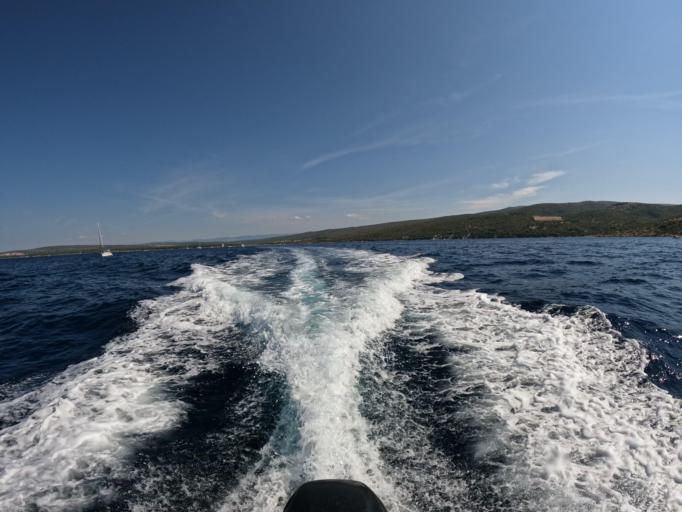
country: HR
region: Primorsko-Goranska
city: Punat
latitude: 44.9870
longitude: 14.6129
